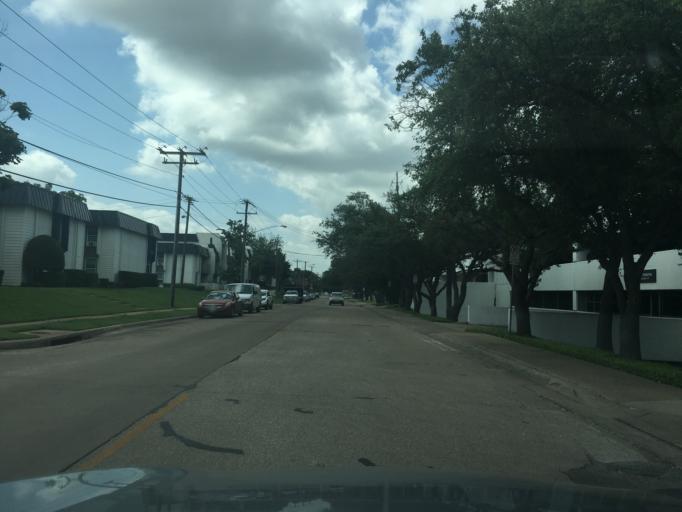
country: US
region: Texas
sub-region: Dallas County
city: Addison
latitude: 32.9252
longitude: -96.8150
